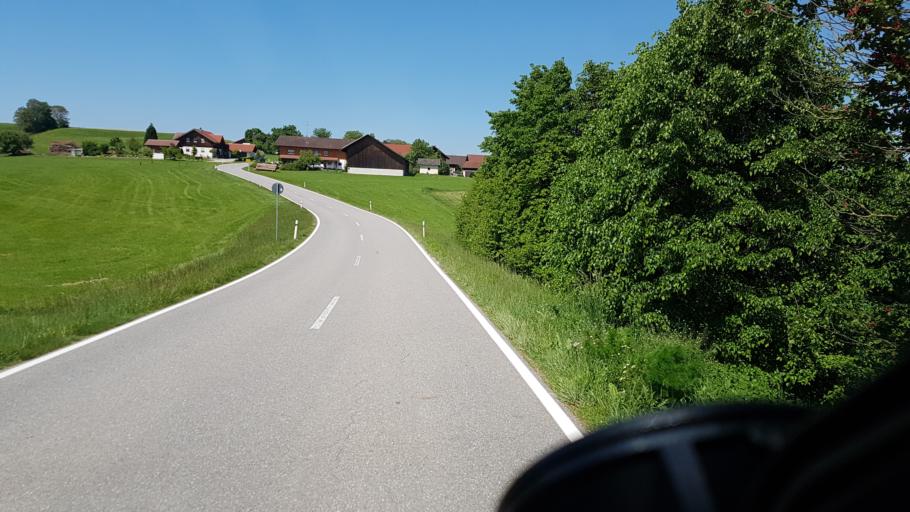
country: DE
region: Bavaria
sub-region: Lower Bavaria
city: Tann
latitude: 48.3413
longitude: 12.8991
